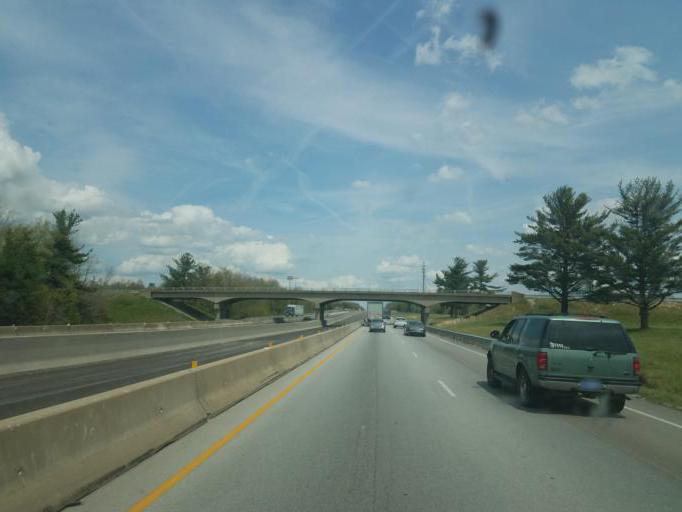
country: US
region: Kentucky
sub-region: Hardin County
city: Elizabethtown
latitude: 37.5950
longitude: -85.8688
